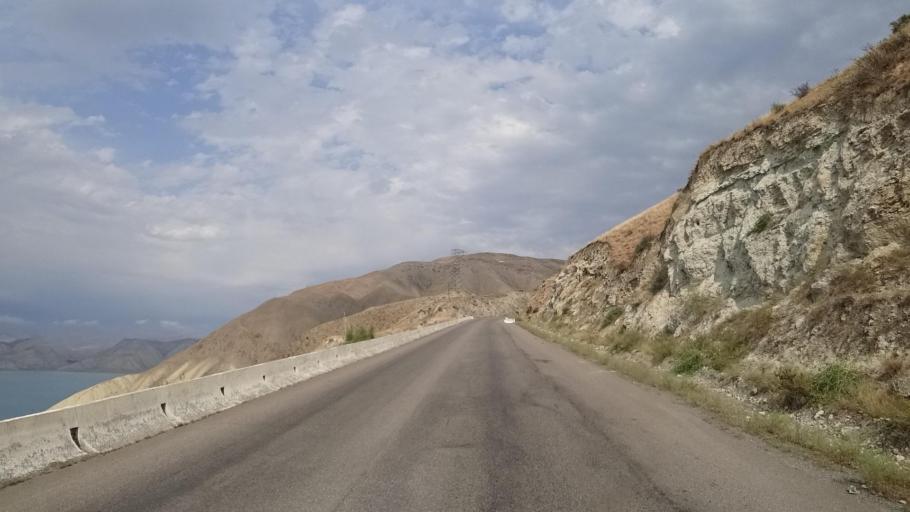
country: KG
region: Jalal-Abad
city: Toktogul
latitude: 41.7792
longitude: 73.0214
